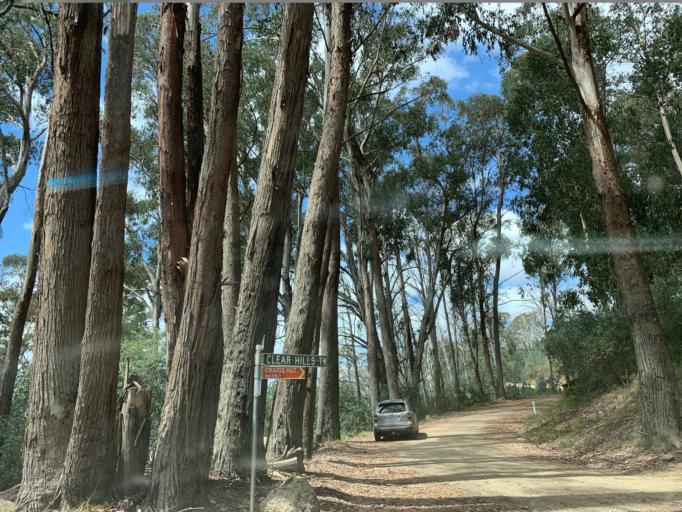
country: AU
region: Victoria
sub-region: Mansfield
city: Mansfield
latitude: -37.0979
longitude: 146.5434
